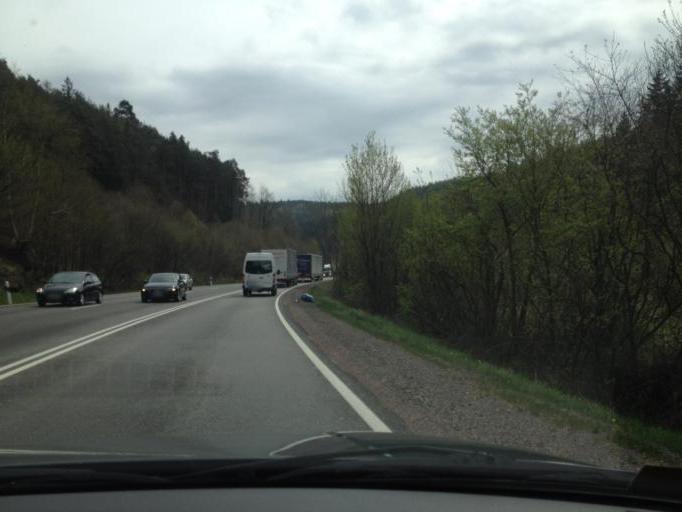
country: DE
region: Rheinland-Pfalz
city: Erfweiler
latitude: 49.2049
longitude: 7.8081
